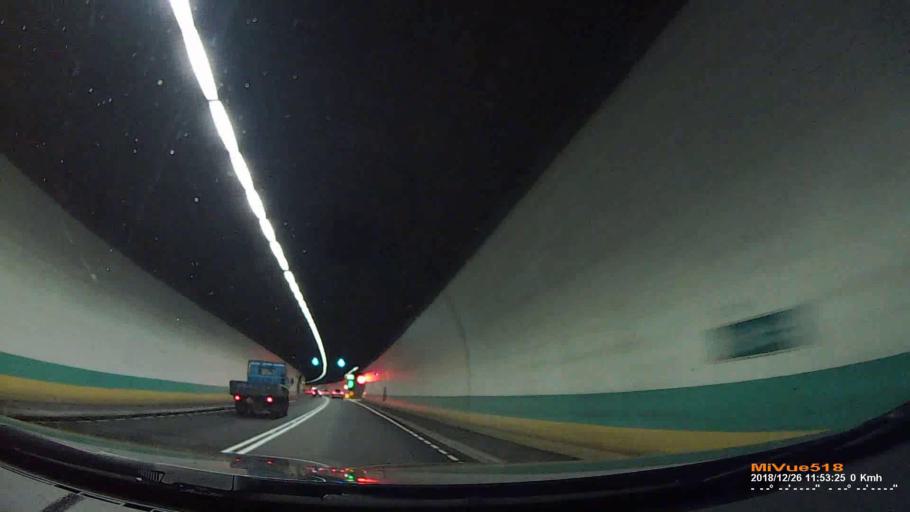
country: TW
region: Taiwan
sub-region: Keelung
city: Keelung
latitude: 24.9587
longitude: 121.6923
